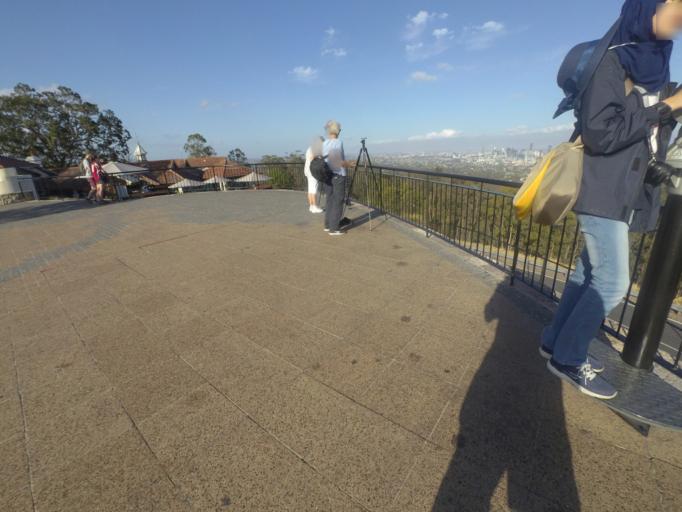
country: AU
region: Queensland
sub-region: Brisbane
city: Taringa
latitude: -27.4851
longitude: 152.9592
